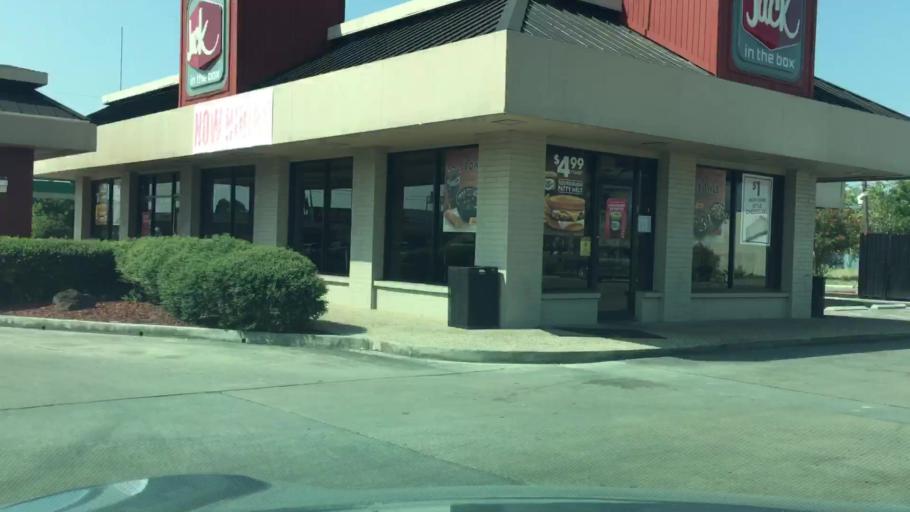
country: US
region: Texas
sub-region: Comal County
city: New Braunfels
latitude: 29.6932
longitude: -98.1110
